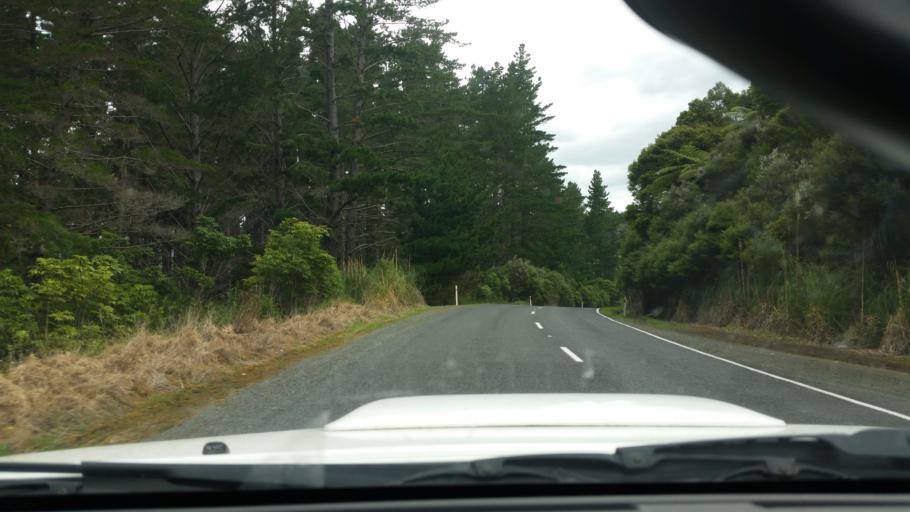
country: NZ
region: Northland
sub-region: Kaipara District
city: Dargaville
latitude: -35.7342
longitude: 173.8645
